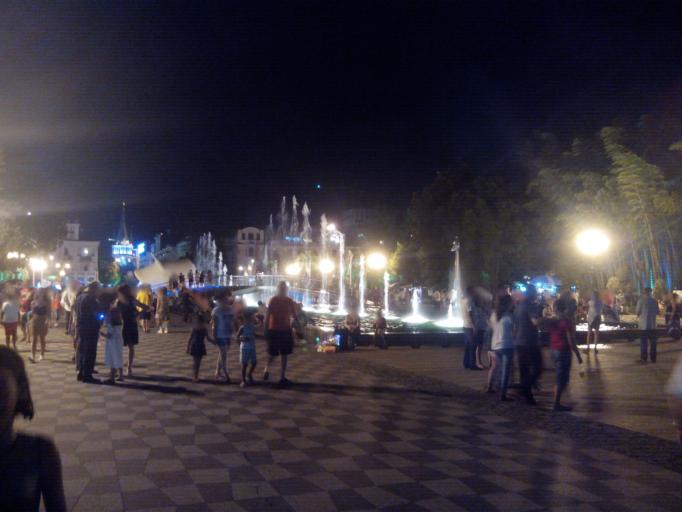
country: GE
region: Ajaria
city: Batumi
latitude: 41.6545
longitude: 41.6351
